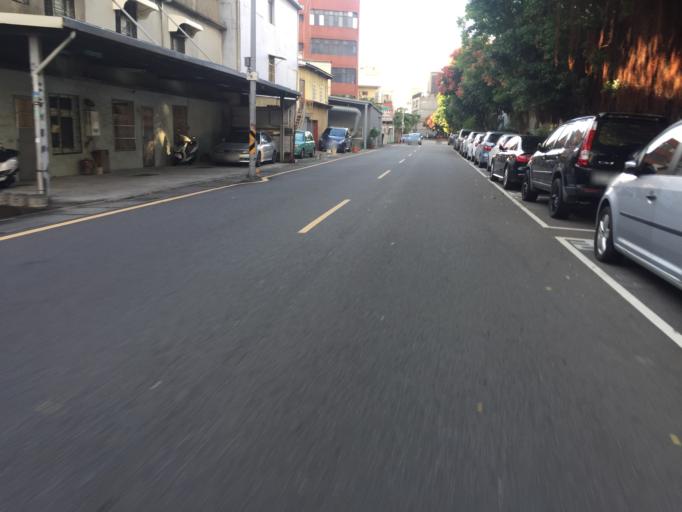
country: TW
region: Taiwan
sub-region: Hsinchu
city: Hsinchu
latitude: 24.8177
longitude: 120.9777
